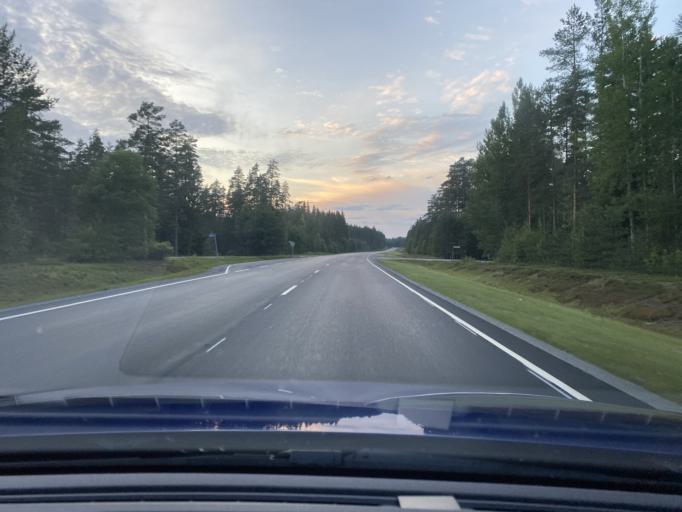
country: FI
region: Satakunta
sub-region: Pohjois-Satakunta
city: Honkajoki
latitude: 62.0071
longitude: 22.2294
